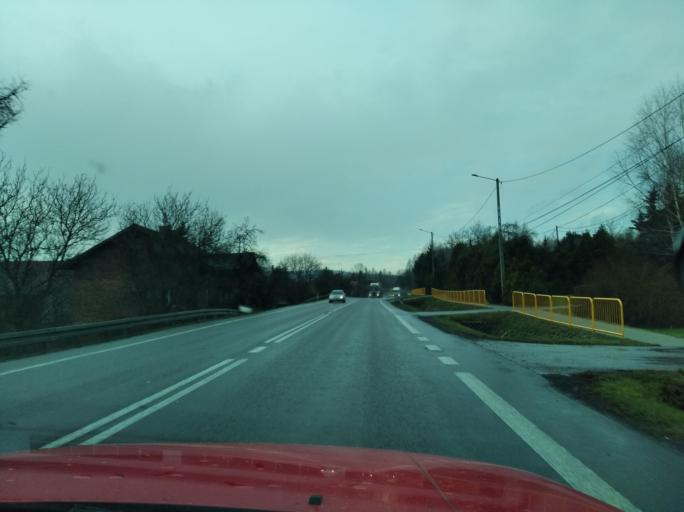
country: PL
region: Subcarpathian Voivodeship
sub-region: Powiat strzyzowski
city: Babica
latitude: 49.9365
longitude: 21.8796
